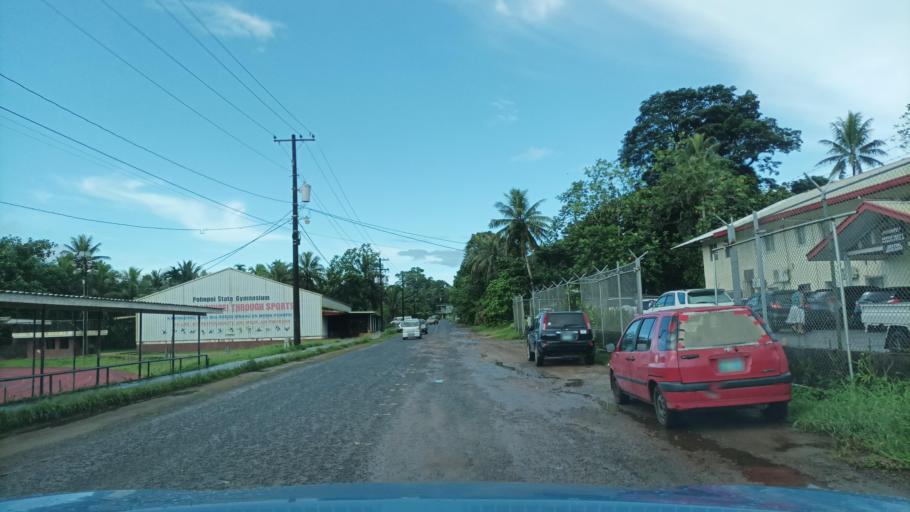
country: FM
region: Pohnpei
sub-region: Kolonia Municipality
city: Kolonia Town
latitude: 6.9506
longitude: 158.2045
